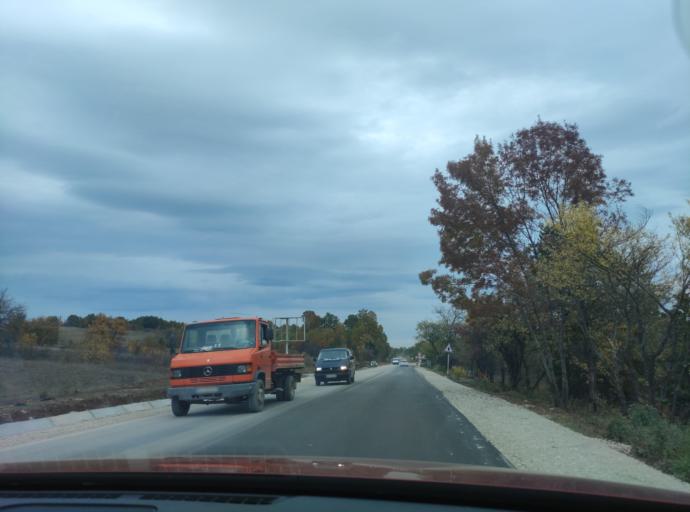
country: BG
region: Montana
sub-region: Obshtina Montana
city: Montana
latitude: 43.3803
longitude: 23.2420
